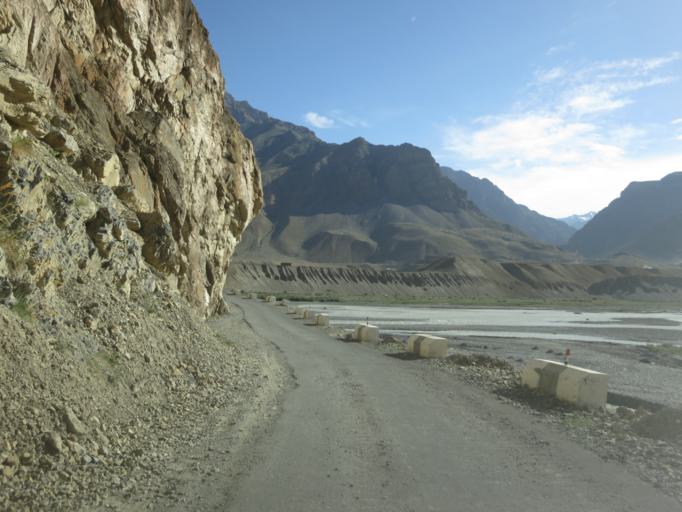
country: IN
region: Himachal Pradesh
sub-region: Shimla
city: Sarahan
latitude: 32.2505
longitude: 78.0514
